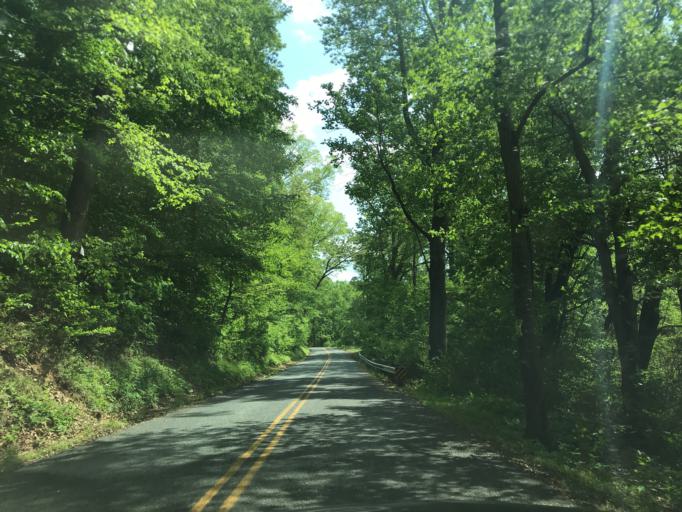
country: US
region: Maryland
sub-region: Harford County
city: Bel Air North
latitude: 39.6027
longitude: -76.3457
